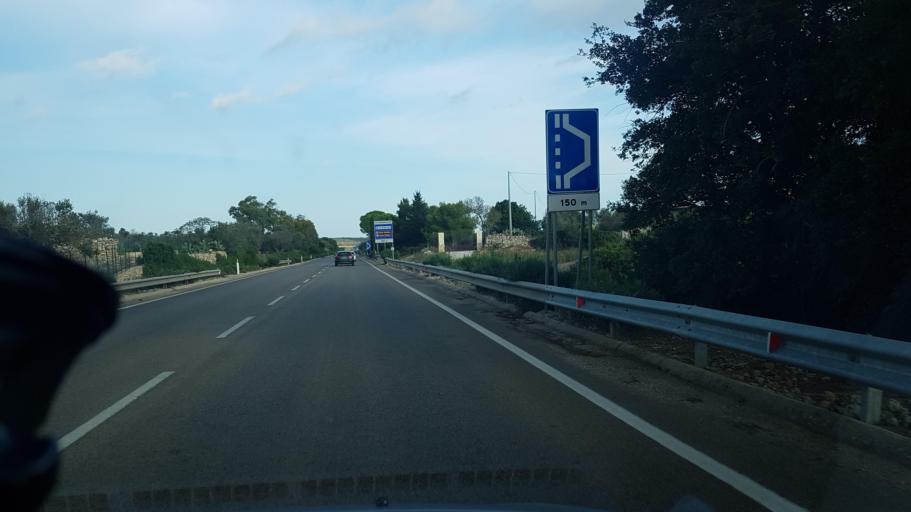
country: IT
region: Apulia
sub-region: Provincia di Lecce
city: Castrignano del Capo
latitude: 39.8204
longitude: 18.3461
